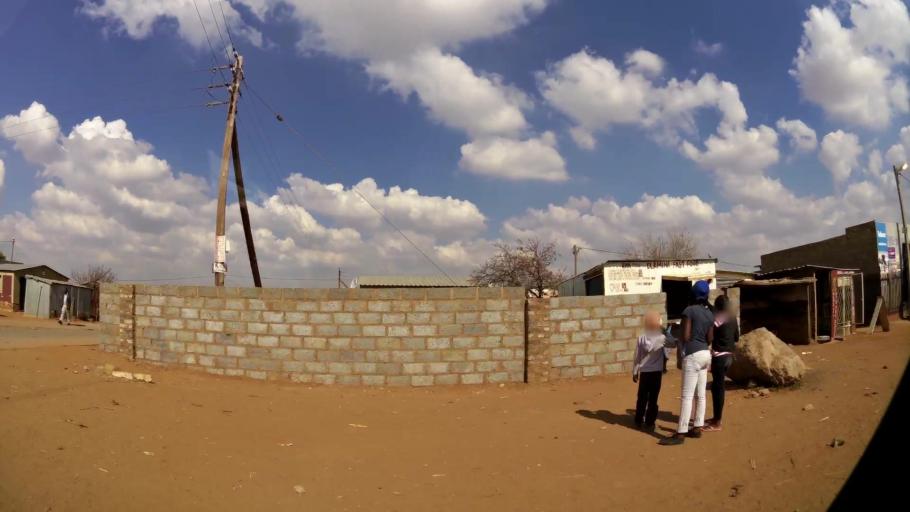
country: ZA
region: Gauteng
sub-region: City of Johannesburg Metropolitan Municipality
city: Roodepoort
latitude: -26.1900
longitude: 27.8691
